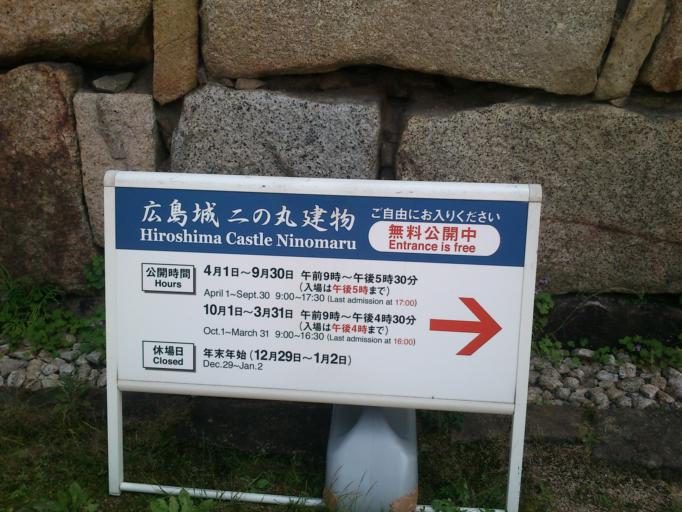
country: JP
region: Hiroshima
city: Hiroshima-shi
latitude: 34.3982
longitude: 132.4591
